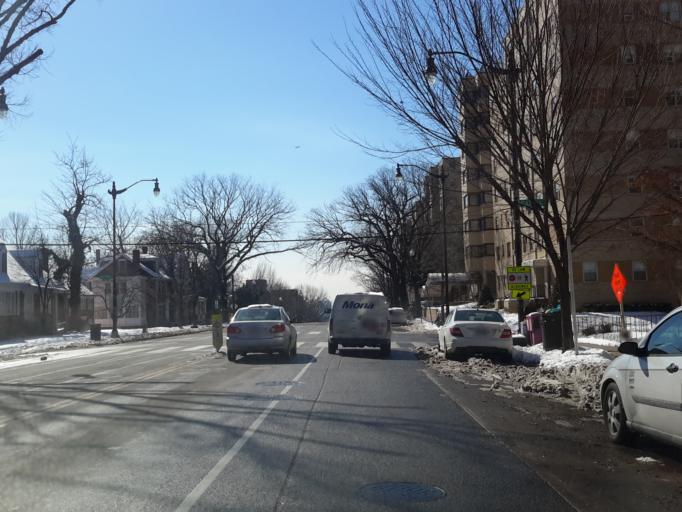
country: US
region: Maryland
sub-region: Montgomery County
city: Friendship Village
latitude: 38.9266
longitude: -77.0732
